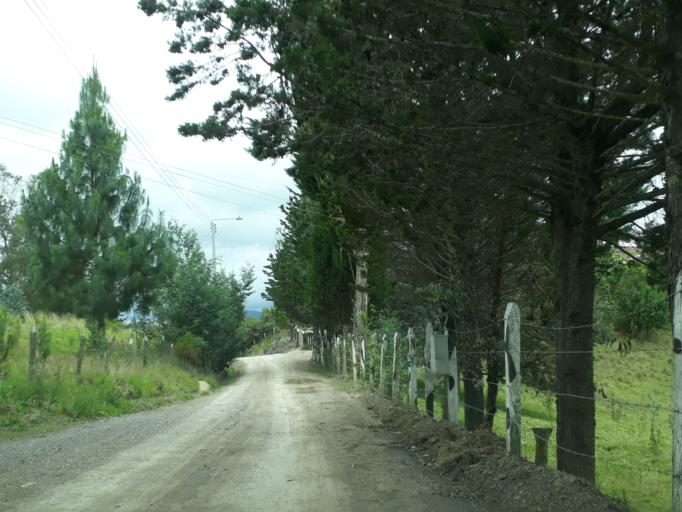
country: CO
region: Cundinamarca
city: Simijaca
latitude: 5.5545
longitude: -73.8205
